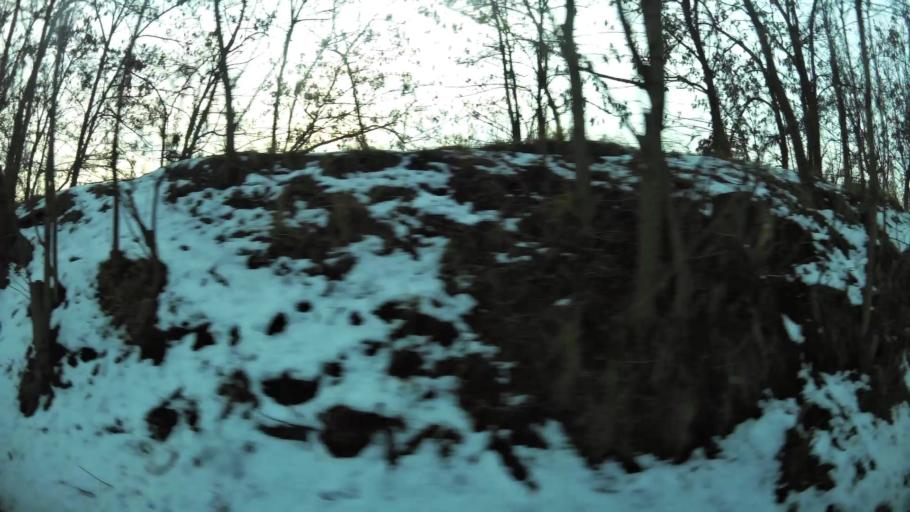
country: MK
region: Aracinovo
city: Arachinovo
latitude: 42.0216
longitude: 21.5594
